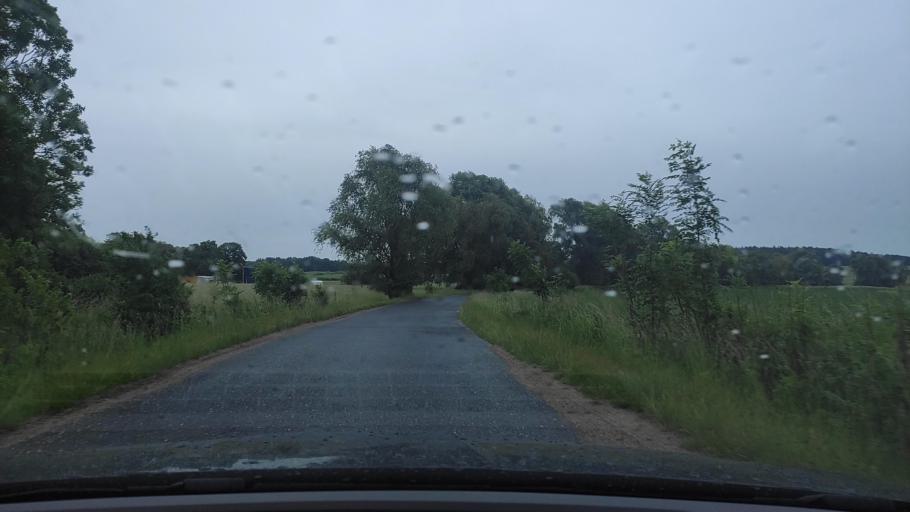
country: PL
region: Greater Poland Voivodeship
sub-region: Powiat poznanski
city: Kobylnica
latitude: 52.4960
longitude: 17.1261
